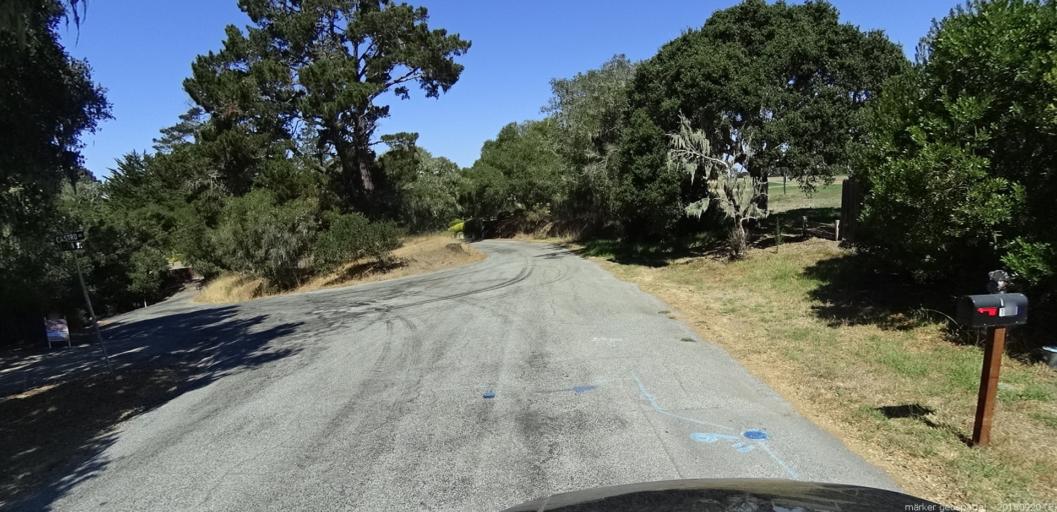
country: US
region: California
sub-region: Monterey County
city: Monterey
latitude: 36.5815
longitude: -121.8716
